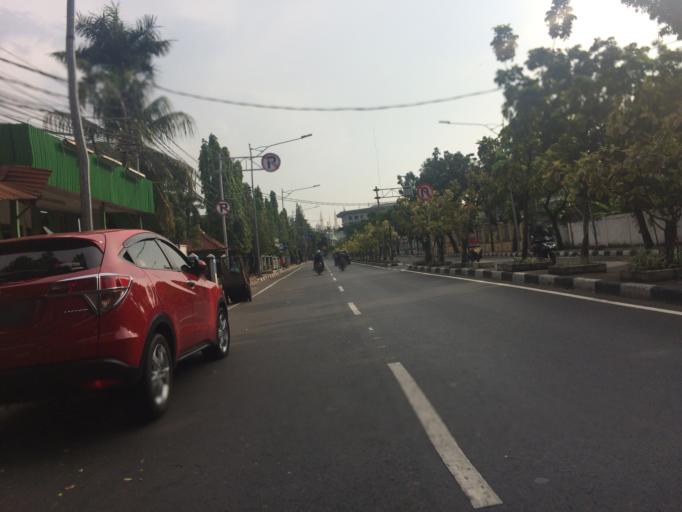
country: ID
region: Jakarta Raya
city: Jakarta
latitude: -6.1667
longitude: 106.8387
